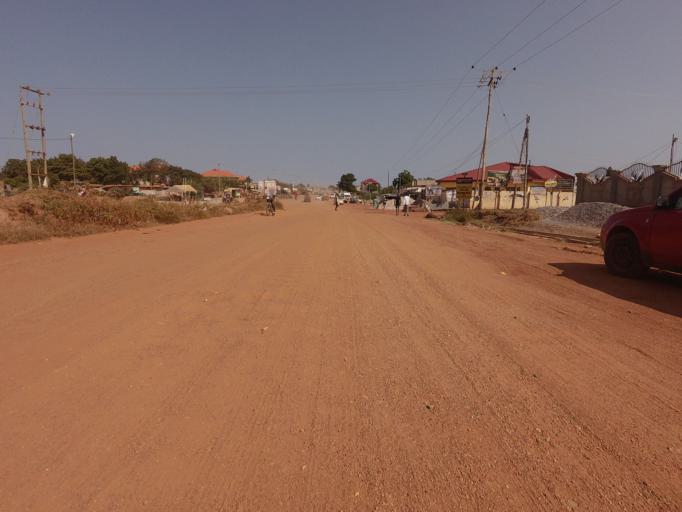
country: GH
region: Greater Accra
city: Teshi Old Town
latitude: 5.6048
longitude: -0.1219
